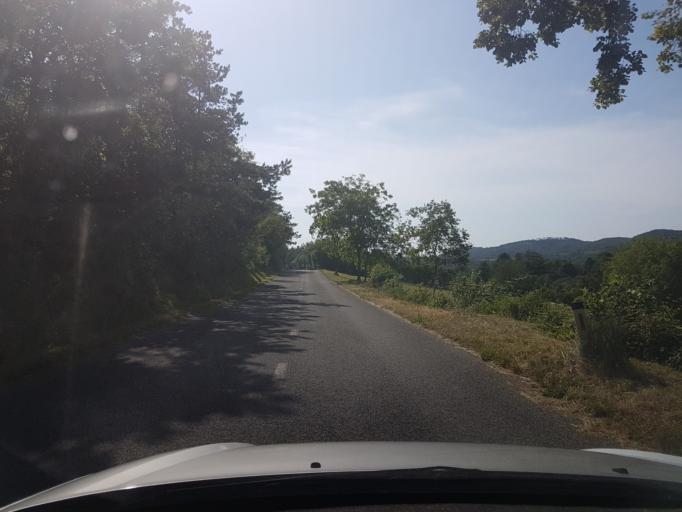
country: SI
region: Vipava
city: Vipava
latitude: 45.7721
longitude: 13.9579
